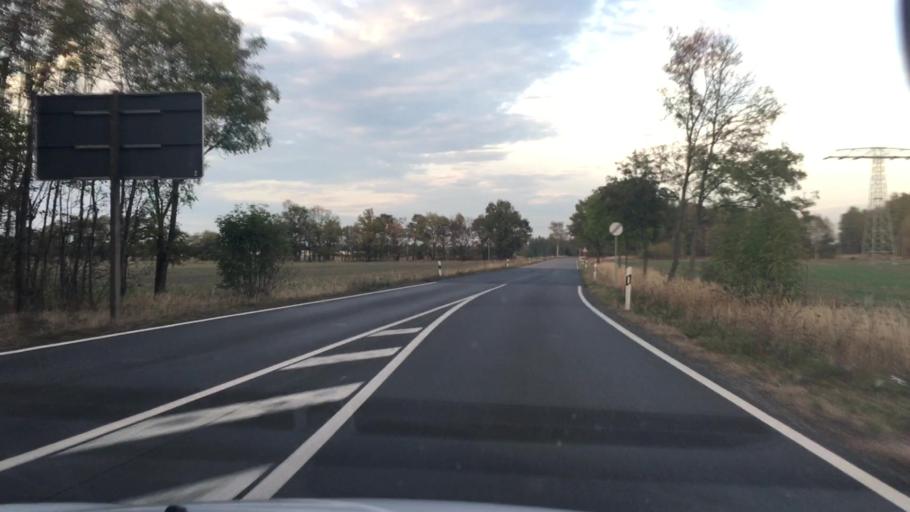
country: DE
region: Brandenburg
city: Grossraschen
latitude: 51.5720
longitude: 14.0796
